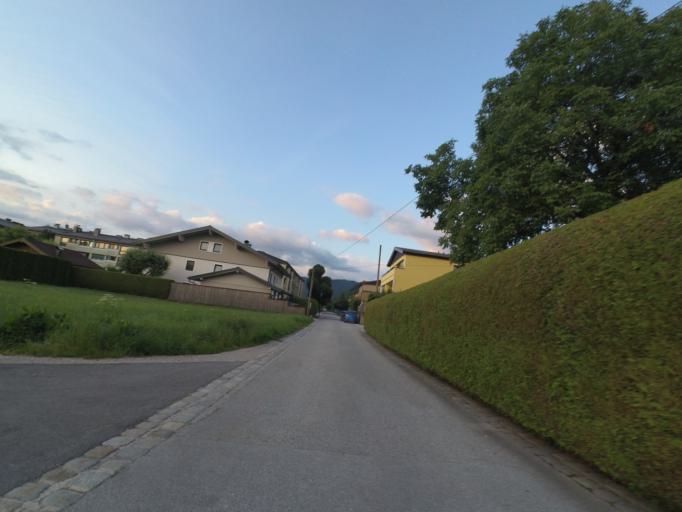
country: AT
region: Salzburg
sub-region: Politischer Bezirk Salzburg-Umgebung
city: Anif
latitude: 47.7365
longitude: 13.0548
